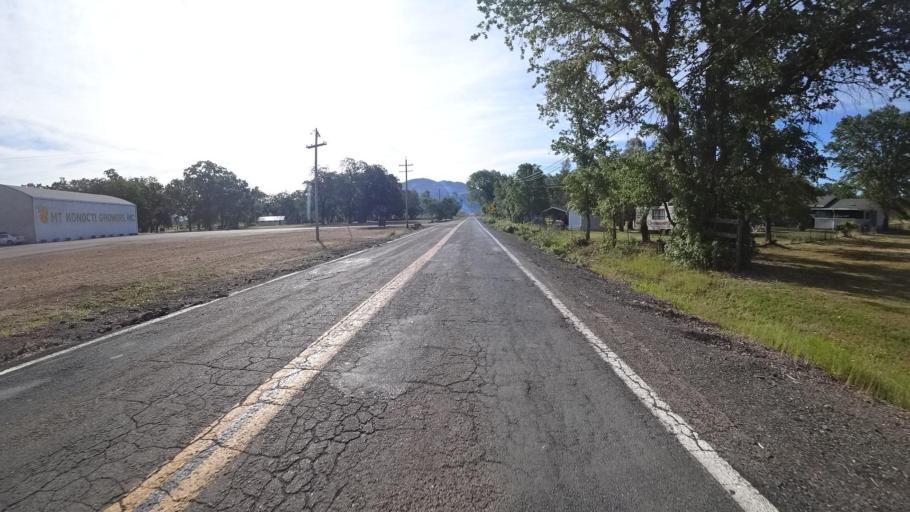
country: US
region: California
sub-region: Lake County
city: Kelseyville
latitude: 38.9944
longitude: -122.8642
